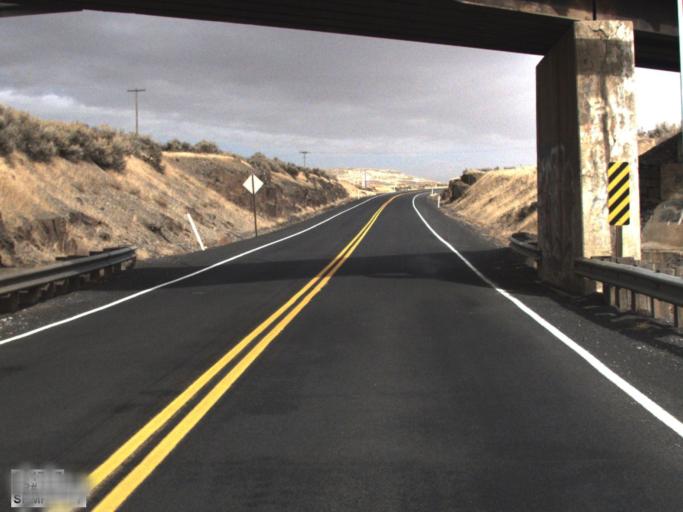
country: US
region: Washington
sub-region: Adams County
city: Ritzville
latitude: 47.3336
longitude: -118.6587
